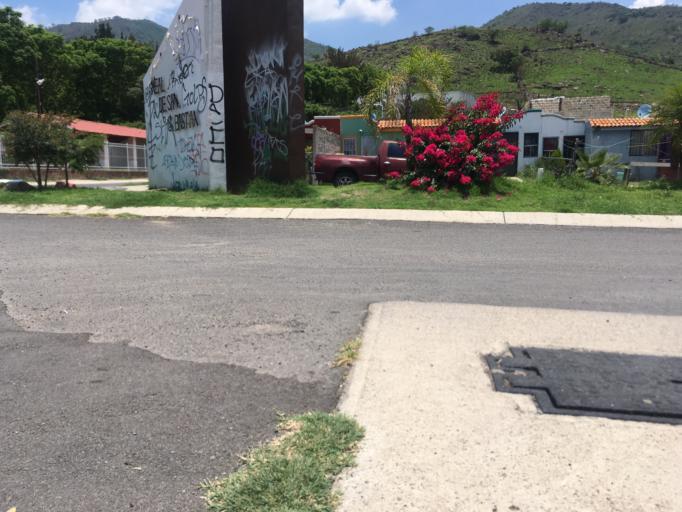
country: MX
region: Jalisco
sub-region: Tlajomulco de Zuniga
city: La Roca
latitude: 20.5145
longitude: -103.4261
